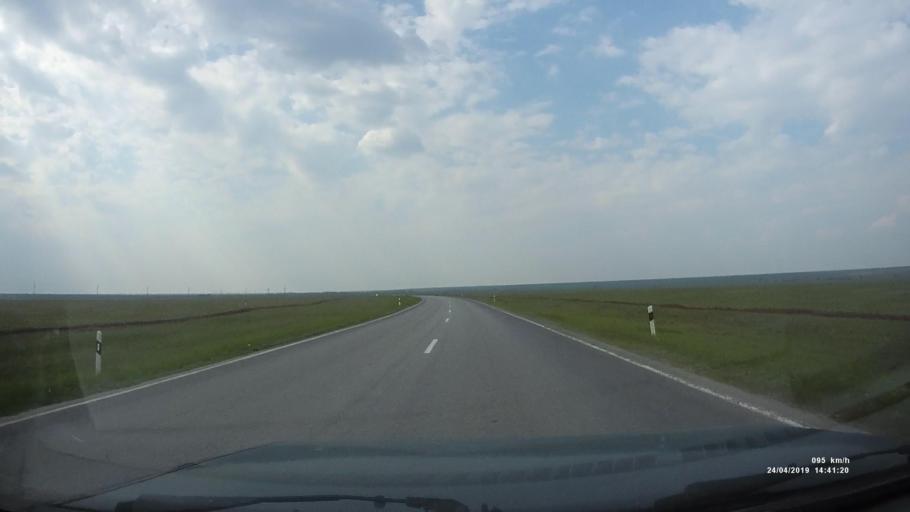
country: RU
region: Rostov
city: Remontnoye
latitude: 46.4441
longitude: 43.8811
